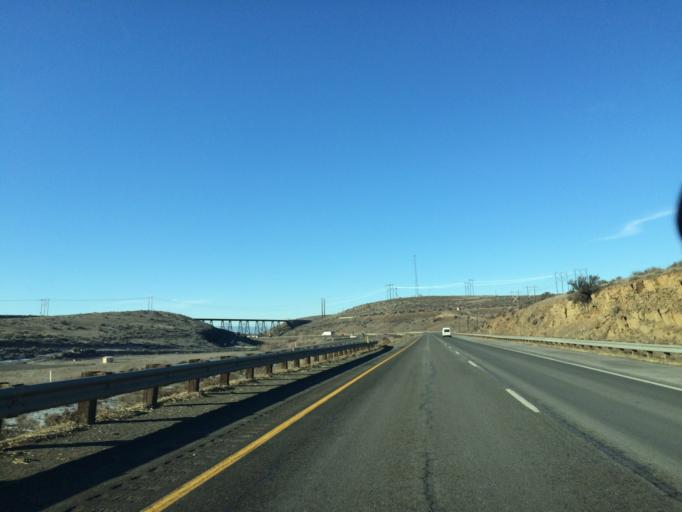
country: US
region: Washington
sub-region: Kittitas County
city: Kittitas
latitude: 46.9543
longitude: -120.2941
